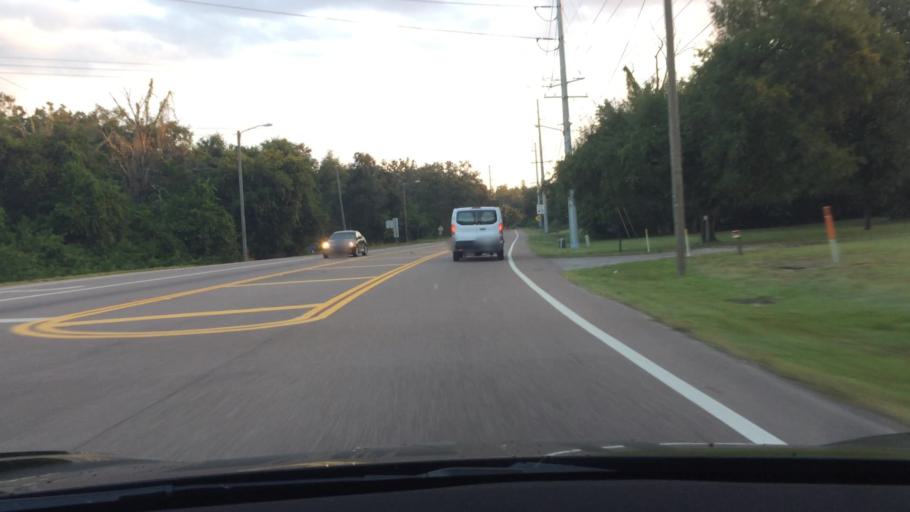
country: US
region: Florida
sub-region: Hillsborough County
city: Citrus Park
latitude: 28.1031
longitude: -82.5806
